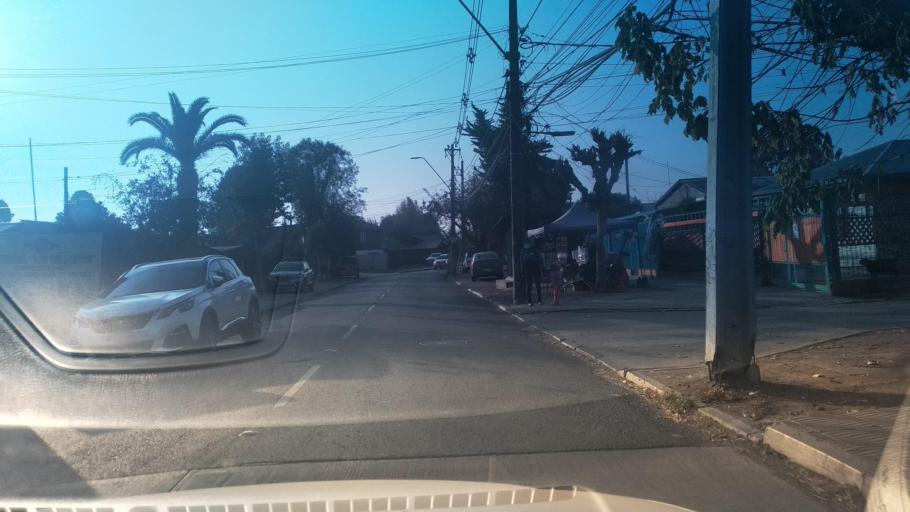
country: CL
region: Santiago Metropolitan
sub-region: Provincia de Santiago
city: Lo Prado
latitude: -33.3661
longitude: -70.7139
